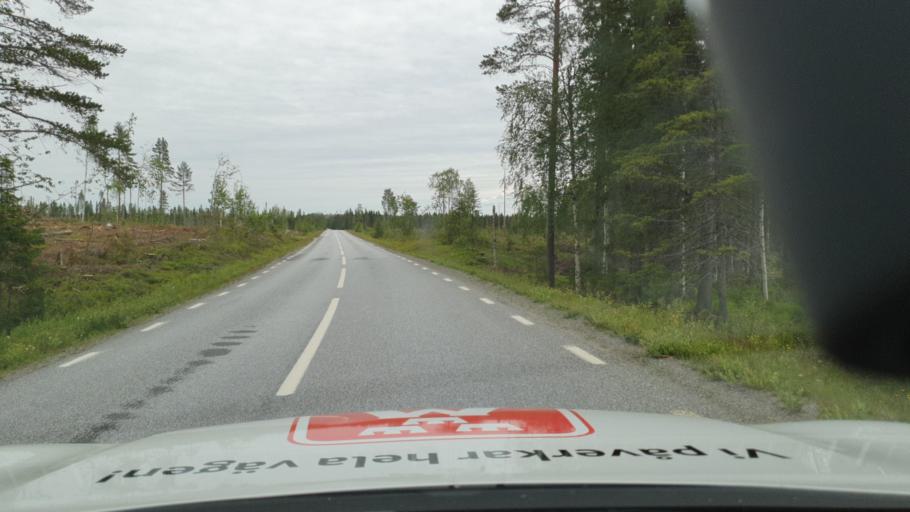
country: SE
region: Vaesterbotten
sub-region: Skelleftea Kommun
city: Burtraesk
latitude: 64.3951
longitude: 20.3125
